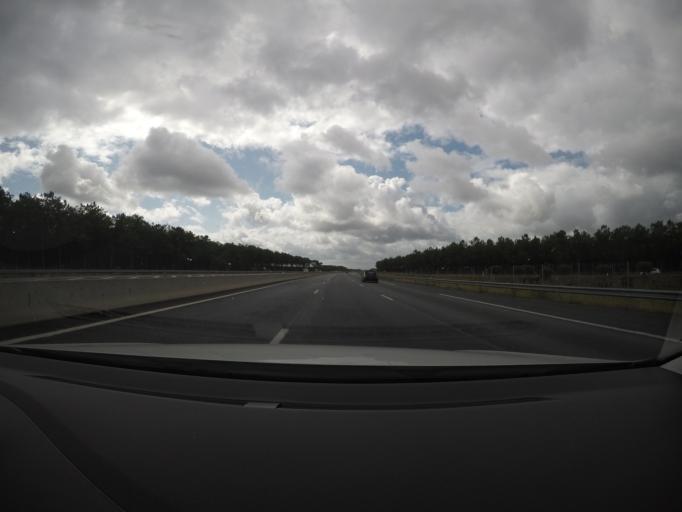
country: FR
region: Aquitaine
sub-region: Departement de la Gironde
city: Belin-Beliet
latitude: 44.4445
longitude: -0.8107
